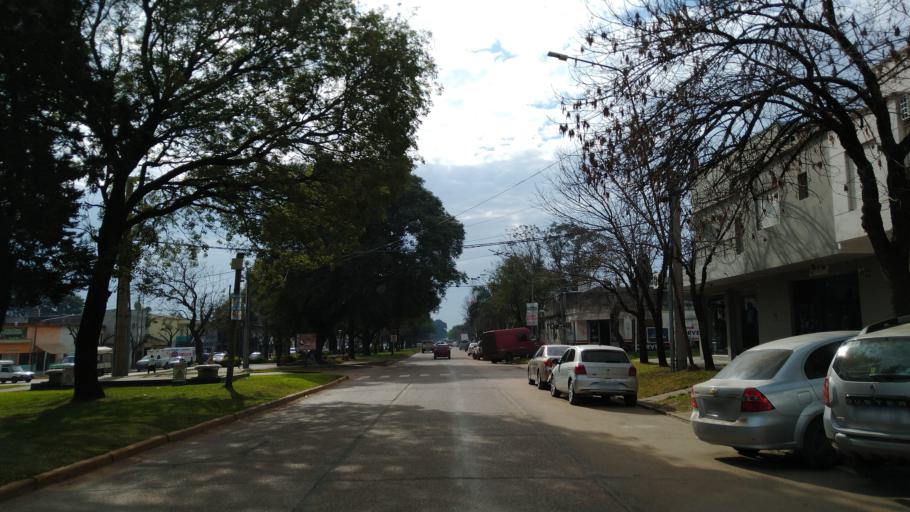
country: AR
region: Entre Rios
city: Chajari
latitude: -30.7574
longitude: -57.9871
